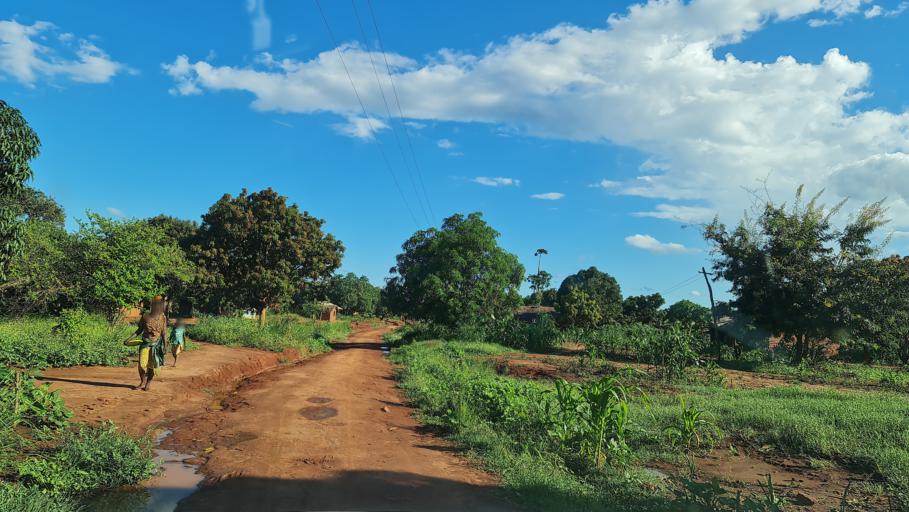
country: MZ
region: Nampula
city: Ilha de Mocambique
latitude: -14.9188
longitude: 40.2174
